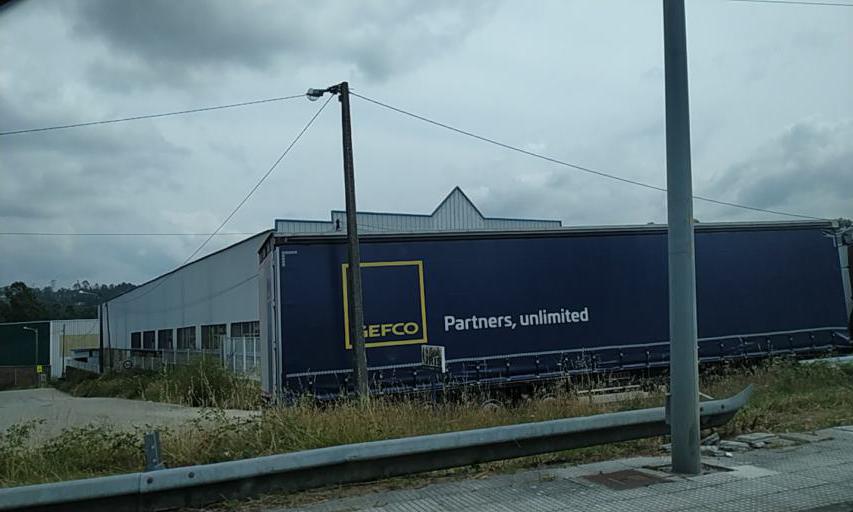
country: ES
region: Galicia
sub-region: Provincia de Pontevedra
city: Tui
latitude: 42.0741
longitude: -8.6288
